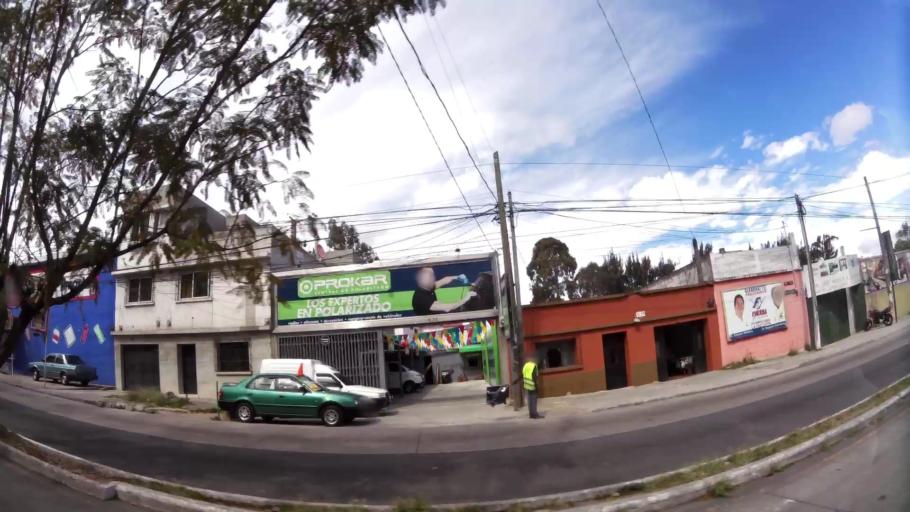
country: GT
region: Guatemala
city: Mixco
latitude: 14.6370
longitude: -90.5824
